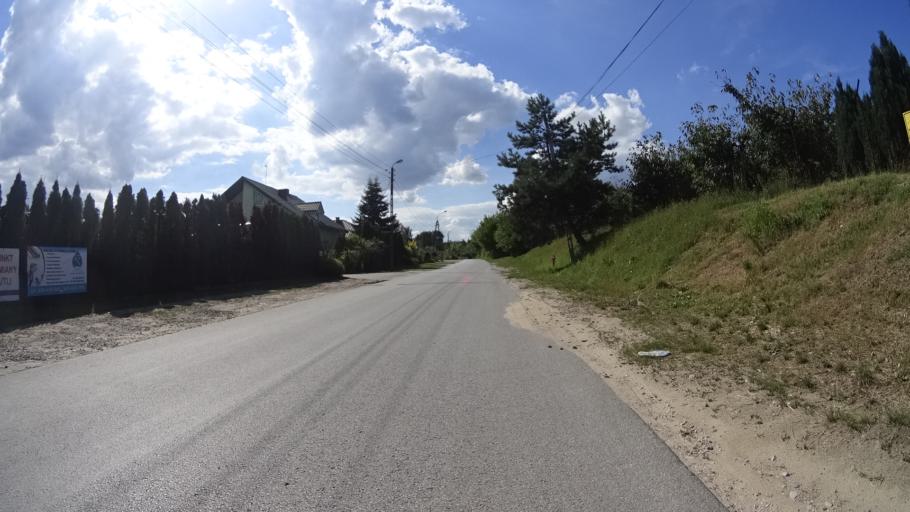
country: PL
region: Masovian Voivodeship
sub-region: Powiat grojecki
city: Mogielnica
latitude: 51.6941
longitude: 20.7179
